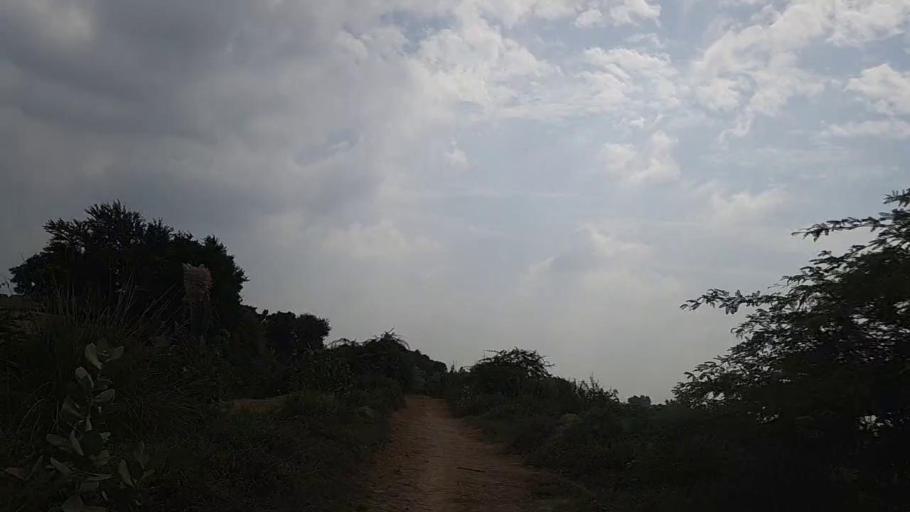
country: PK
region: Sindh
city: Mirpur Batoro
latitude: 24.6122
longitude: 68.1358
